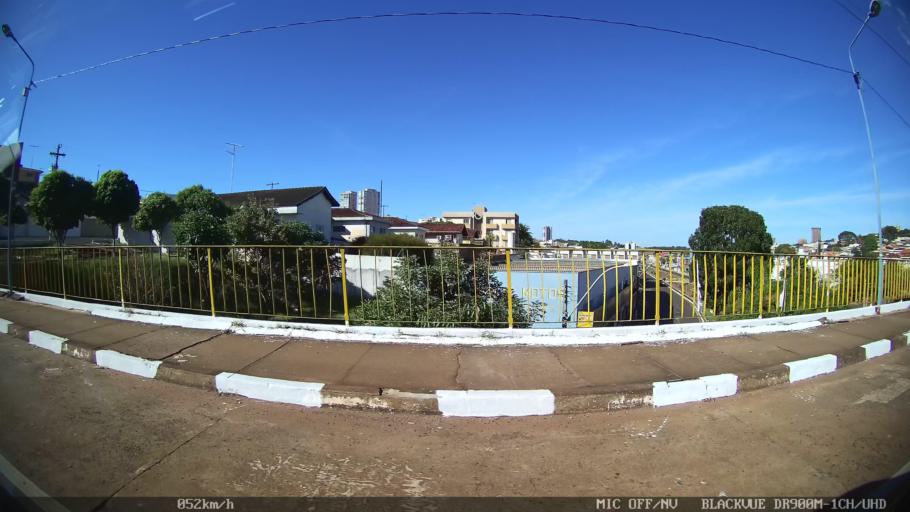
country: BR
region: Sao Paulo
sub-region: Franca
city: Franca
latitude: -20.5423
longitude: -47.4082
